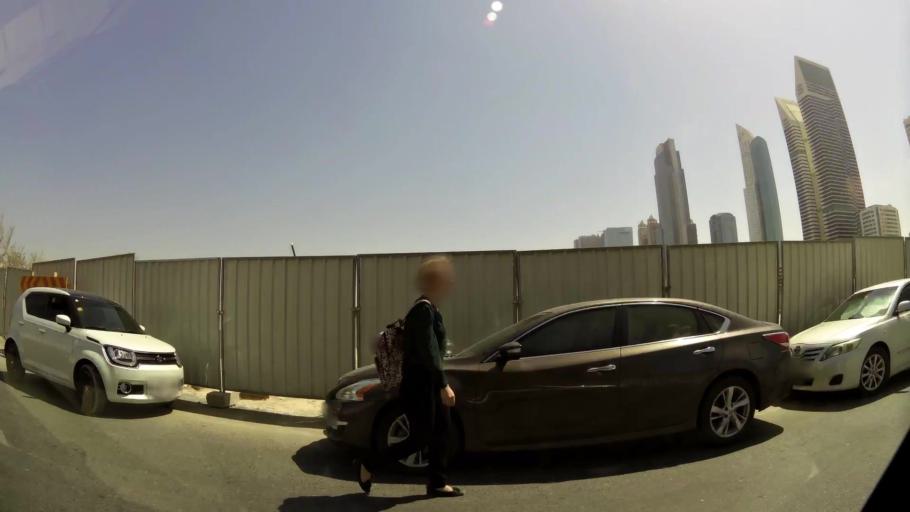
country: AE
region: Ash Shariqah
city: Sharjah
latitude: 25.2230
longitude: 55.2780
